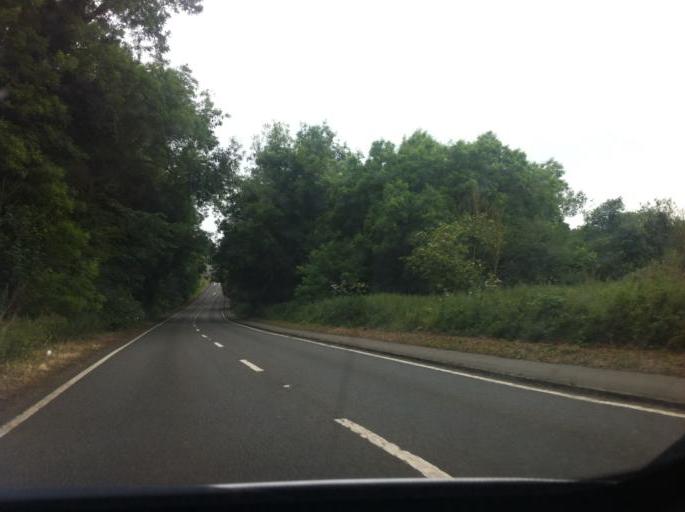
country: GB
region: England
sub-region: Northamptonshire
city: Earls Barton
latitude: 52.2635
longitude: -0.8005
